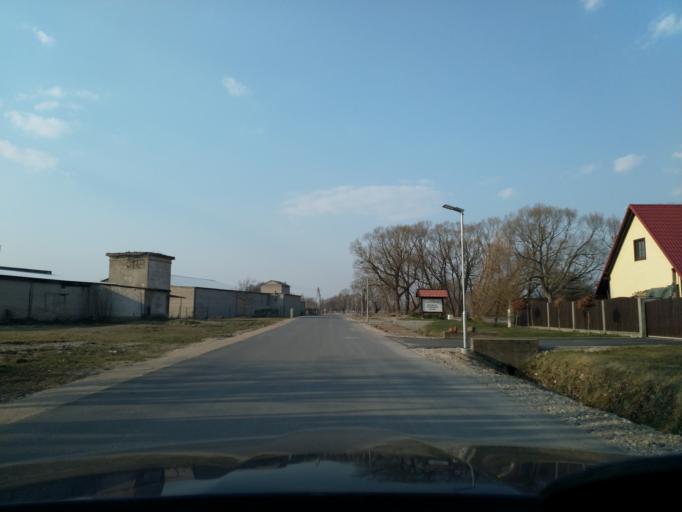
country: LV
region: Grobina
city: Grobina
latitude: 56.5340
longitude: 21.1824
